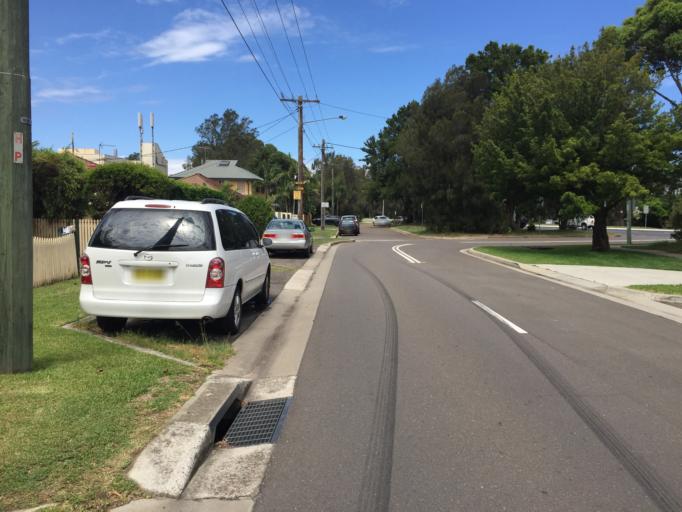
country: AU
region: New South Wales
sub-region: Pittwater
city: North Narrabeen
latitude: -33.7101
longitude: 151.2936
